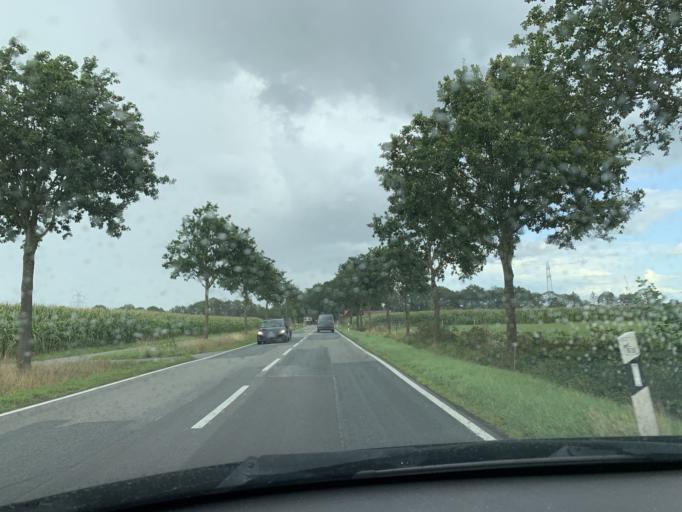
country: DE
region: Lower Saxony
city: Wiefelstede
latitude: 53.2927
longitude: 8.0382
